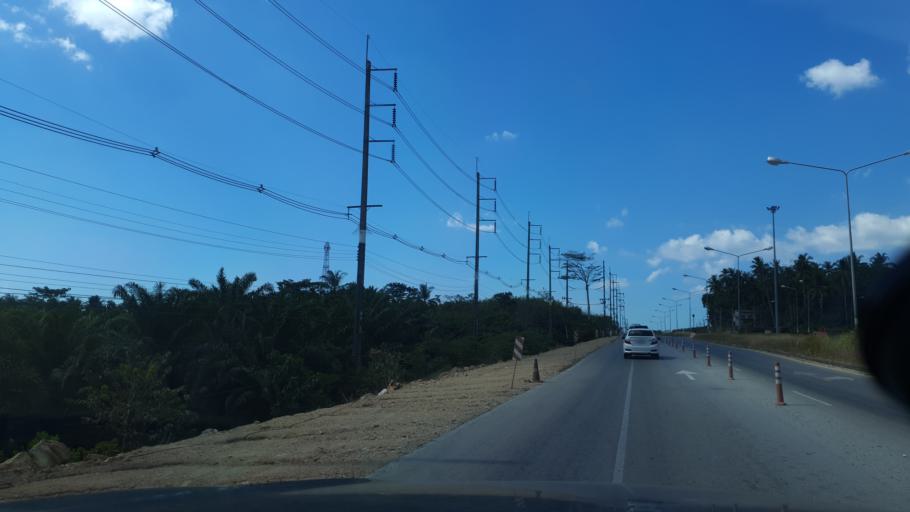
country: TH
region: Phangnga
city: Ban Khao Lak
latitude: 8.5352
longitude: 98.2822
